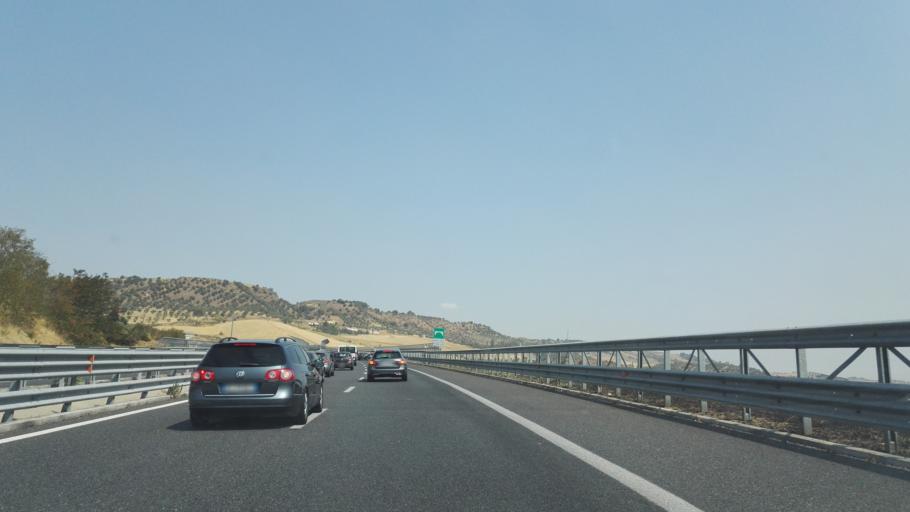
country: IT
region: Calabria
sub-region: Provincia di Cosenza
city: Tarsia
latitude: 39.5915
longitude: 16.2459
